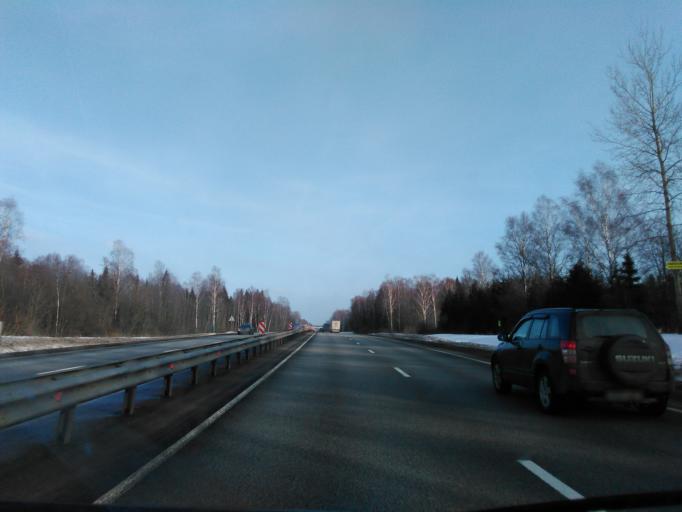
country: RU
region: Smolensk
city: Vyaz'ma
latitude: 55.1911
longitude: 33.9567
